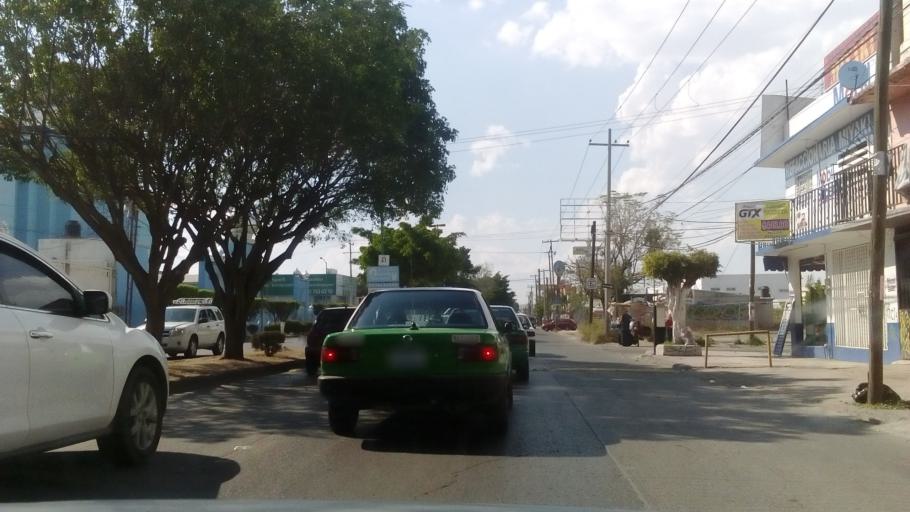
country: MX
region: Guanajuato
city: Leon
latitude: 21.1305
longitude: -101.6560
